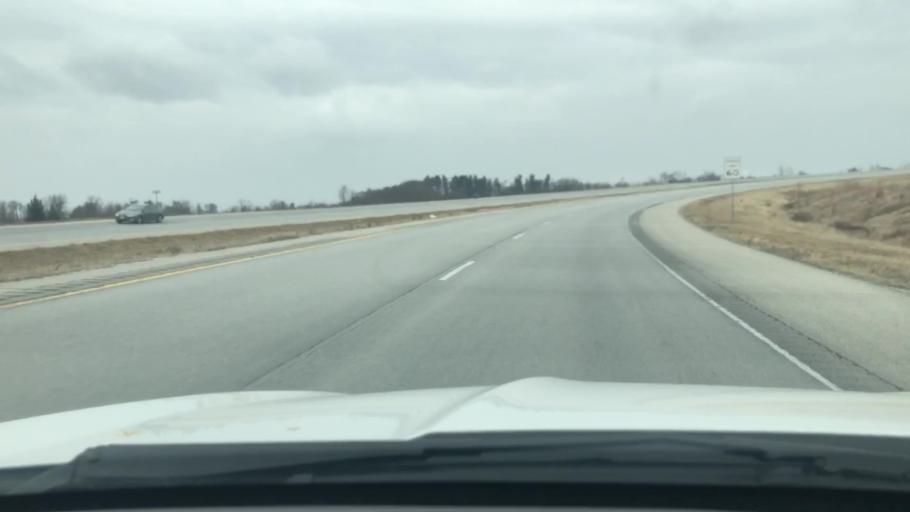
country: US
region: Indiana
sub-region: Cass County
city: Georgetown
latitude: 40.7075
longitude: -86.4551
